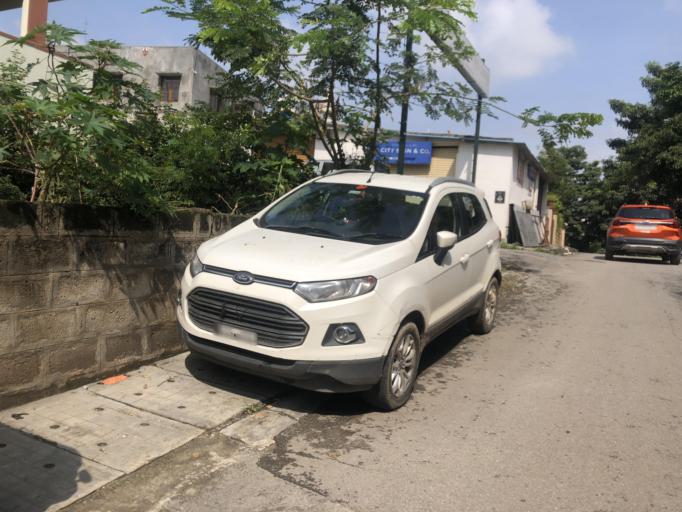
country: IN
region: Karnataka
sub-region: Bangalore Urban
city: Bangalore
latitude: 12.9212
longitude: 77.5284
